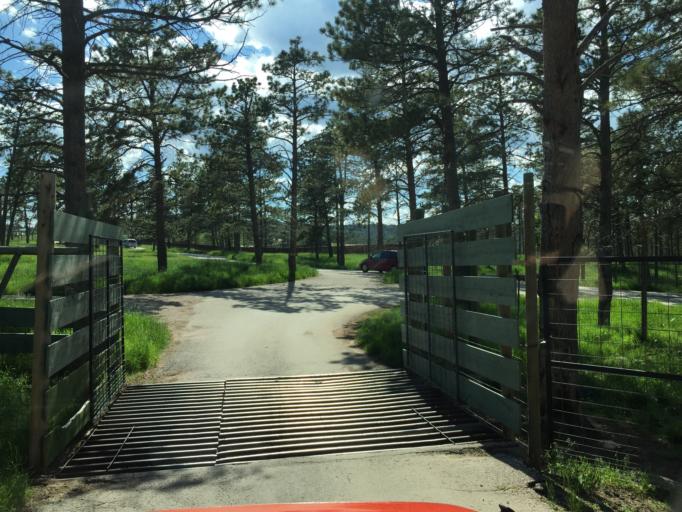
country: US
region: South Dakota
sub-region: Pennington County
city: Colonial Pine Hills
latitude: 43.9804
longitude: -103.2947
